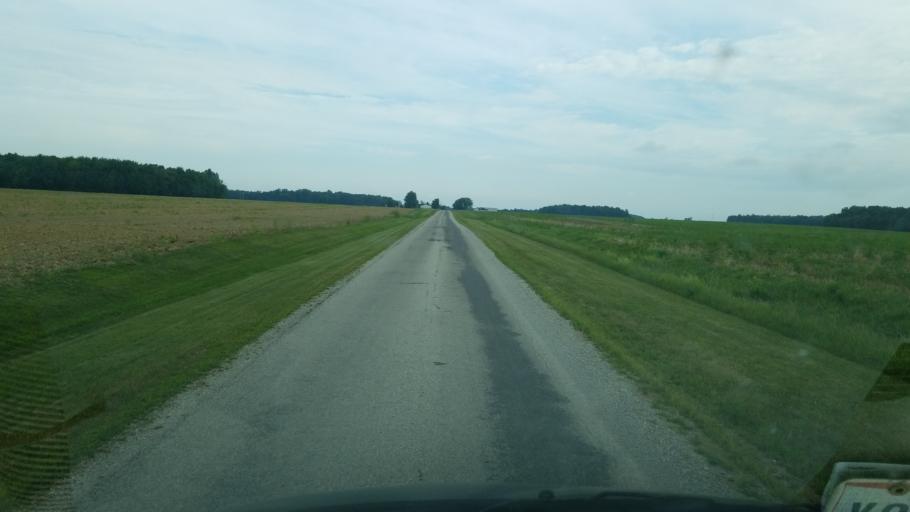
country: US
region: Ohio
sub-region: Crawford County
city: Bucyrus
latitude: 40.9654
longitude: -83.0551
